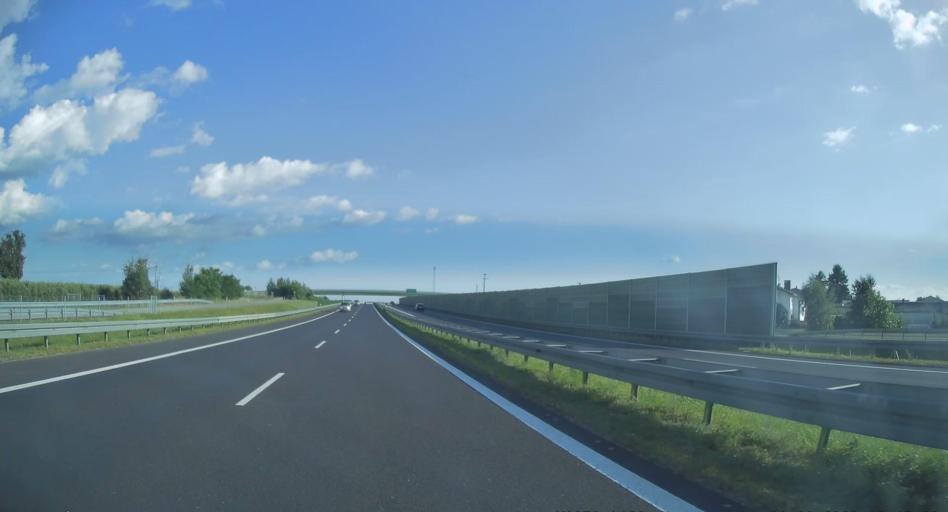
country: PL
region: Masovian Voivodeship
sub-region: Powiat grojecki
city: Jasieniec
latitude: 51.7895
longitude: 20.8929
